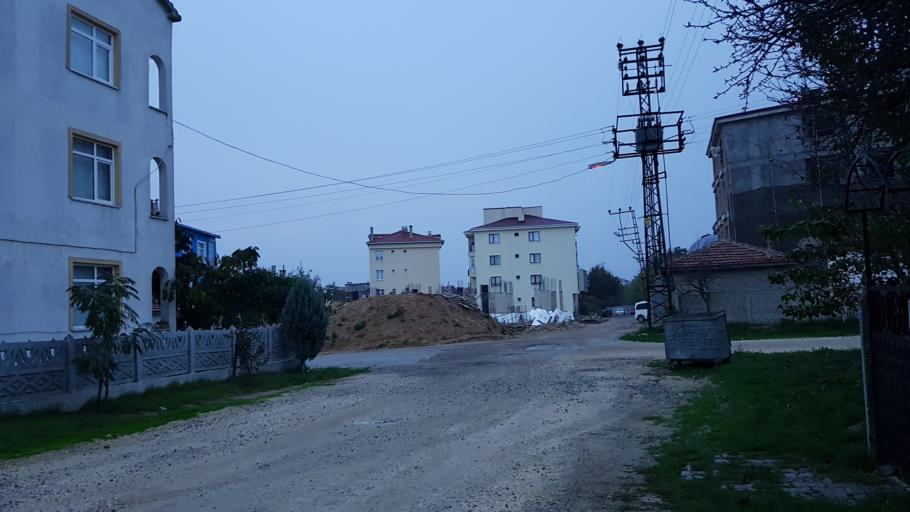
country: TR
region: Tekirdag
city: Saray
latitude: 41.4507
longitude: 27.9297
